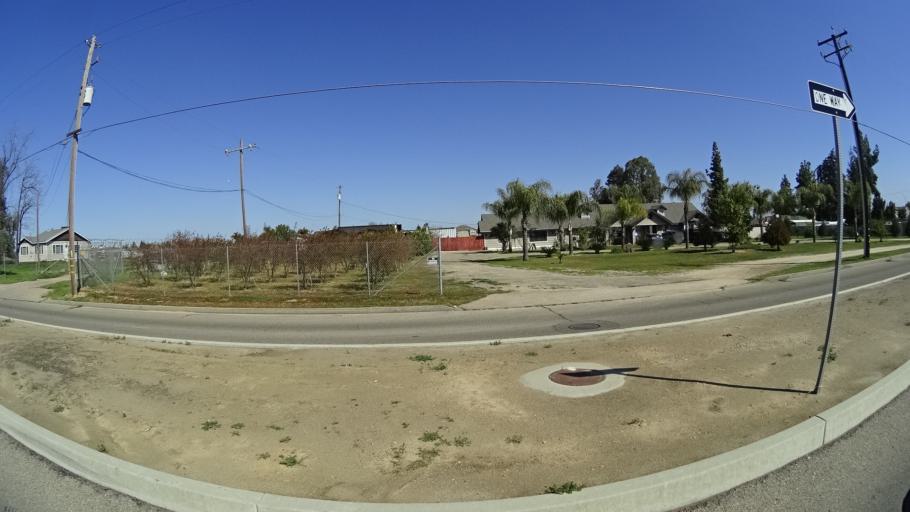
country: US
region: California
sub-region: Fresno County
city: West Park
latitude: 36.7645
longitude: -119.8909
